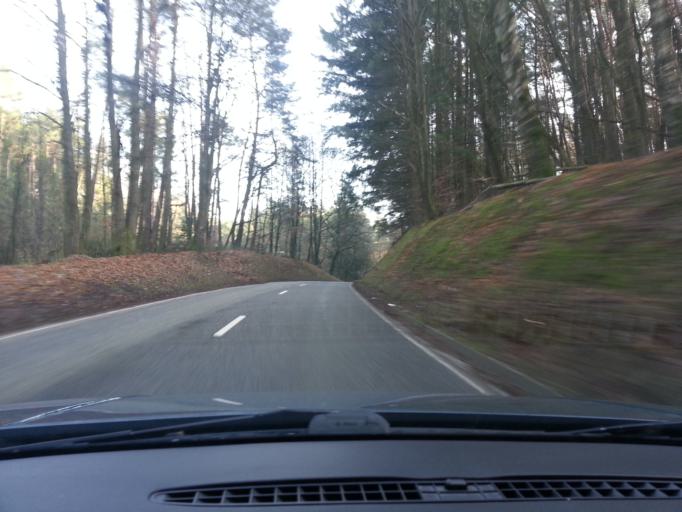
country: DE
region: Rheinland-Pfalz
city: Hauenstein
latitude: 49.1831
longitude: 7.8722
